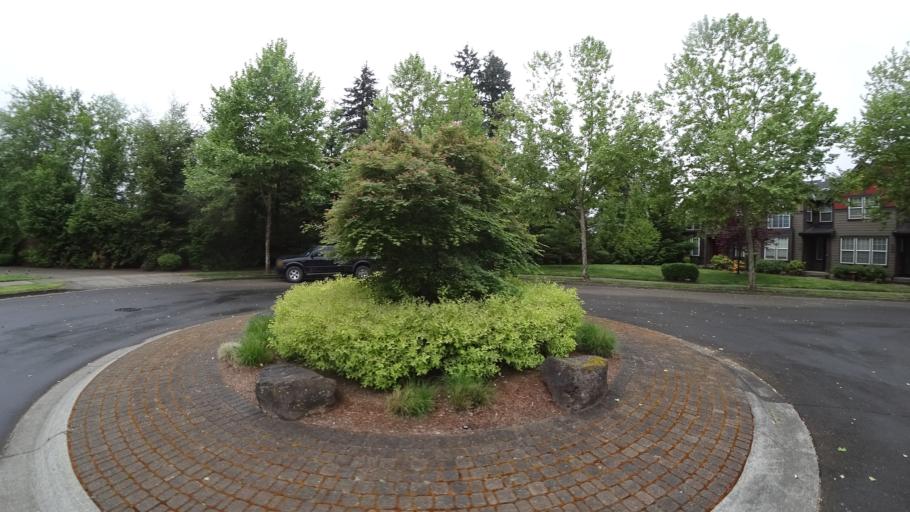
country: US
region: Oregon
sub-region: Washington County
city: Rockcreek
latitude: 45.5281
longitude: -122.9031
